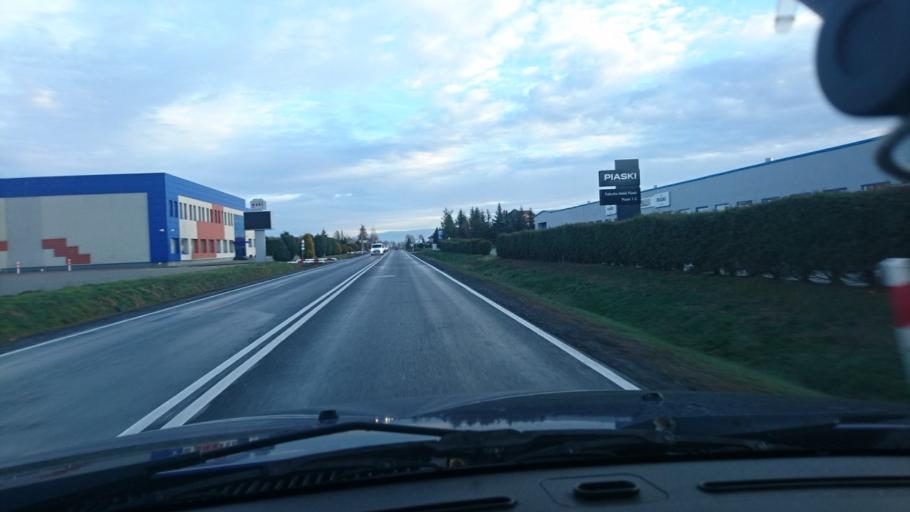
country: PL
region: Greater Poland Voivodeship
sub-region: Powiat kepinski
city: Leka Opatowska
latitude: 51.2293
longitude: 18.0784
